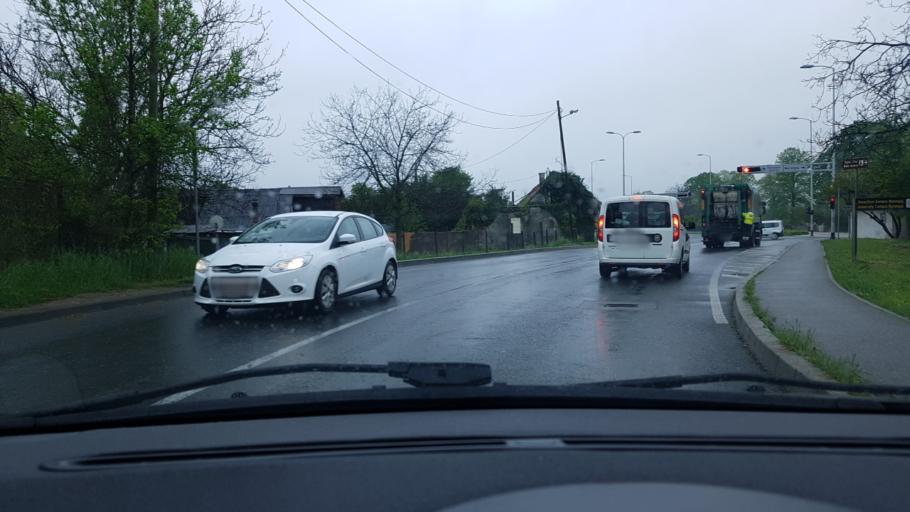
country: HR
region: Grad Zagreb
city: Dubrava
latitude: 45.8065
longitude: 16.0497
